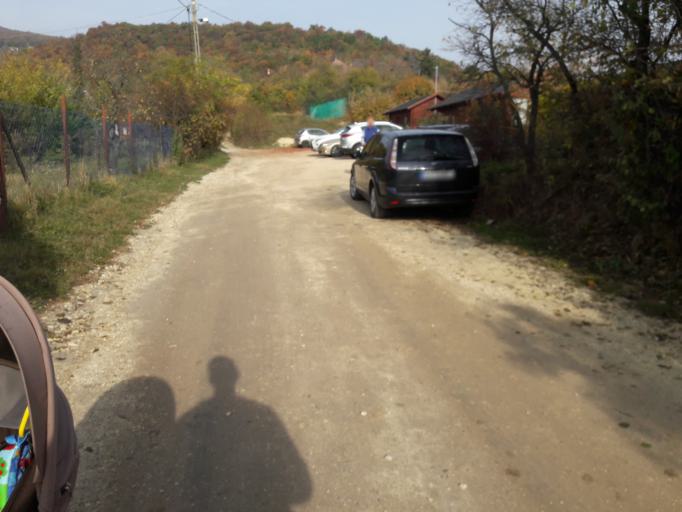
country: HU
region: Pest
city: Budaors
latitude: 47.4714
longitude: 18.9810
